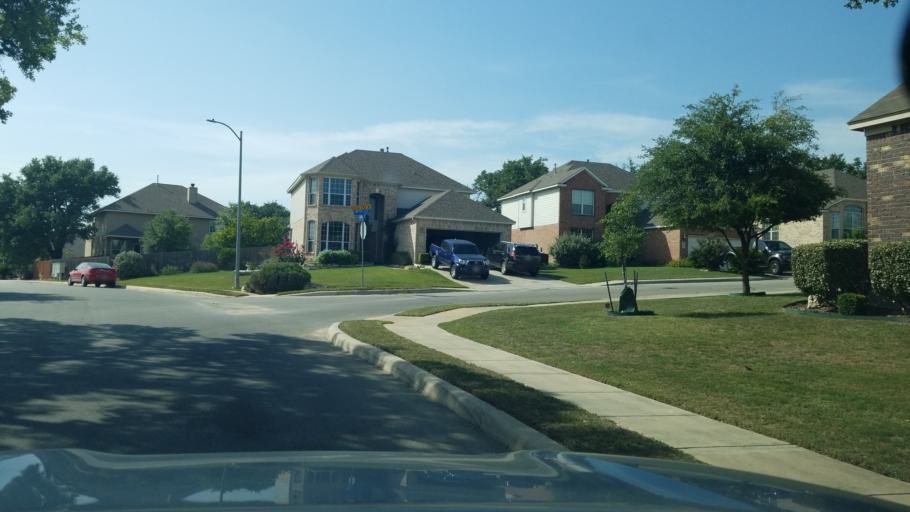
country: US
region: Texas
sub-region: Bexar County
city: Timberwood Park
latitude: 29.6937
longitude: -98.4766
